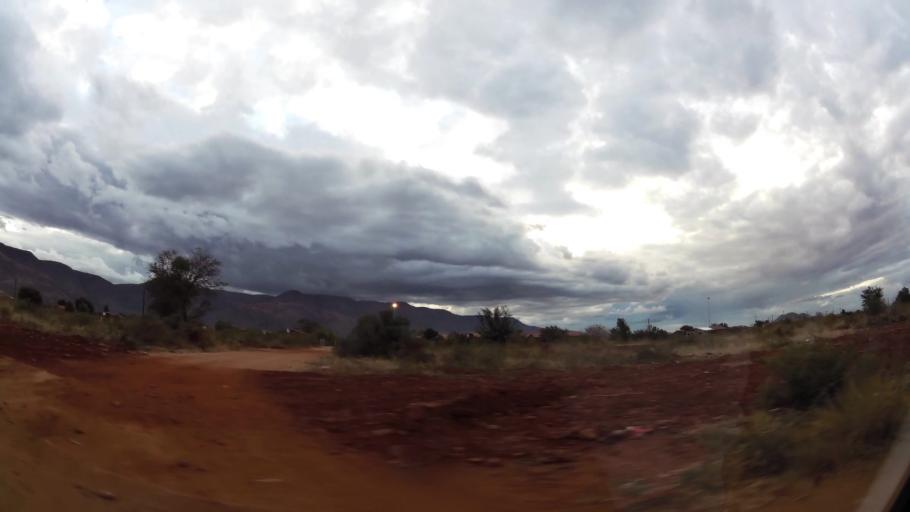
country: ZA
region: Limpopo
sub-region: Waterberg District Municipality
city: Mokopane
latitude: -24.1966
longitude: 28.9881
